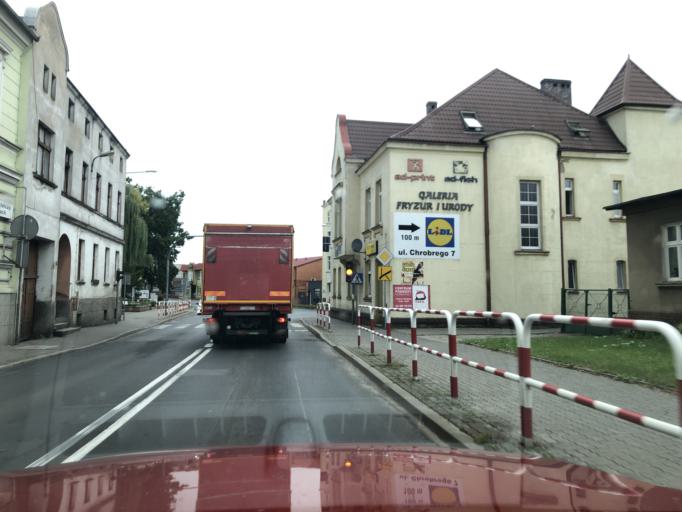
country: PL
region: Greater Poland Voivodeship
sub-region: Powiat szamotulski
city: Wronki
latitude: 52.7075
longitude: 16.3793
